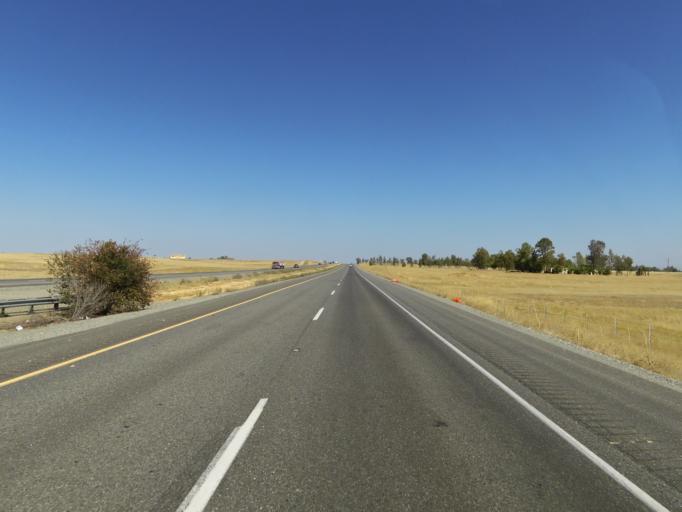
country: US
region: California
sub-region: Tehama County
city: Corning
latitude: 39.8568
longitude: -122.1999
